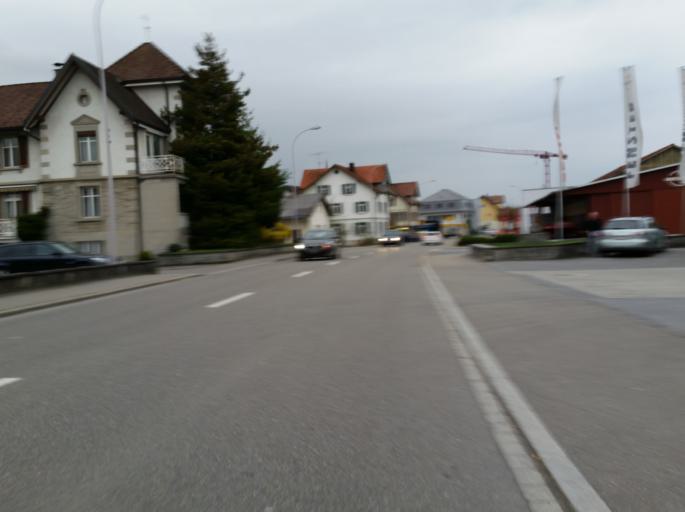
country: CH
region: Saint Gallen
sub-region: Wahlkreis Rheintal
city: Sankt Margrethen
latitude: 47.4485
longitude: 9.6399
